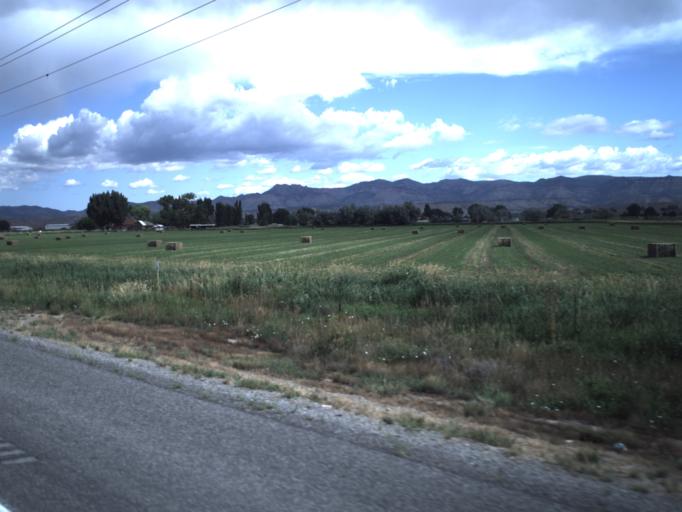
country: US
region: Utah
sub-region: Carbon County
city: Wellington
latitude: 39.5669
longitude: -110.7756
